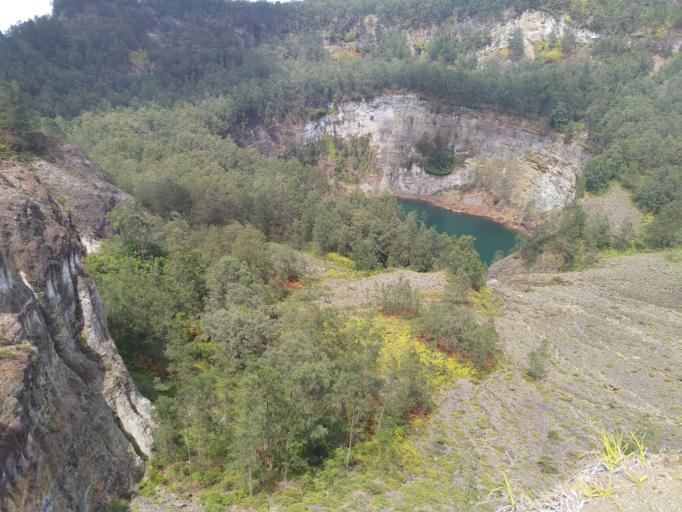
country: ID
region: East Nusa Tenggara
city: Koanara
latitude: -8.7650
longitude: 121.8121
